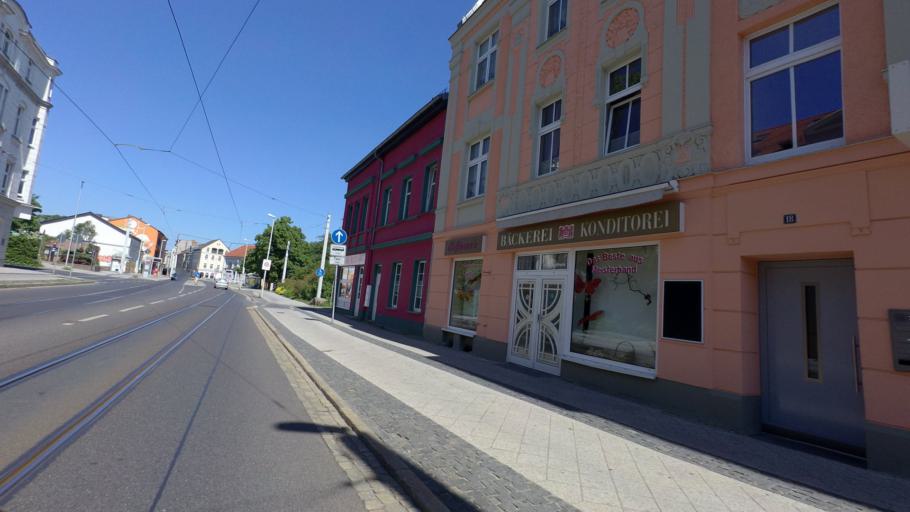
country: DE
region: Brandenburg
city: Cottbus
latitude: 51.7529
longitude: 14.3334
